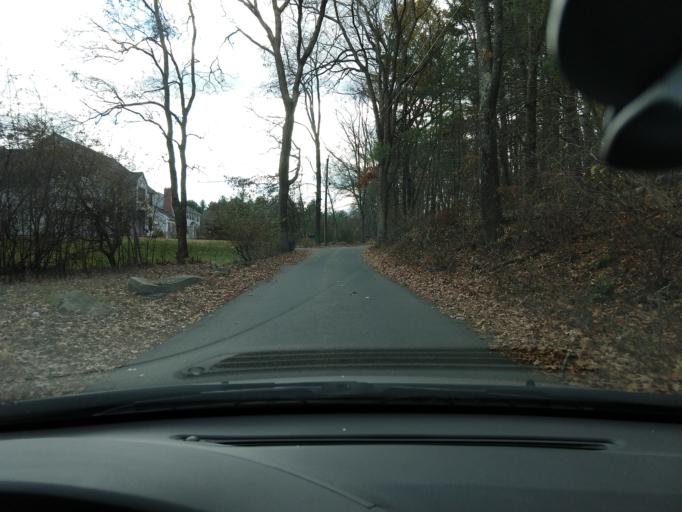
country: US
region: Massachusetts
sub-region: Middlesex County
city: Wayland
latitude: 42.3988
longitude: -71.3756
